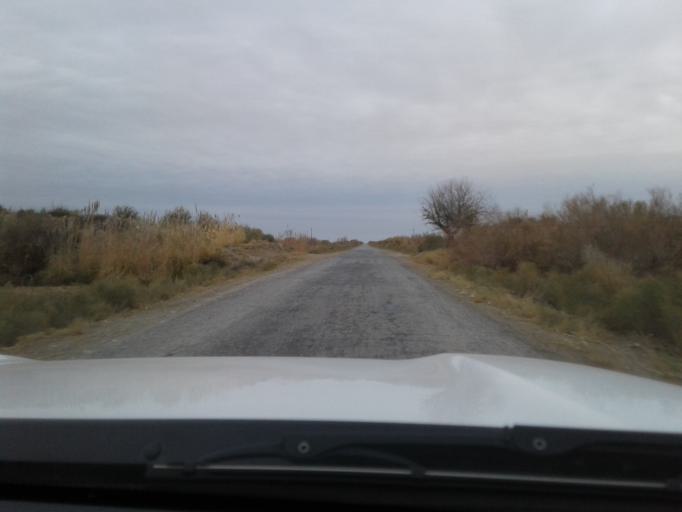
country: TM
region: Mary
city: Mary
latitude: 38.1606
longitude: 61.7744
